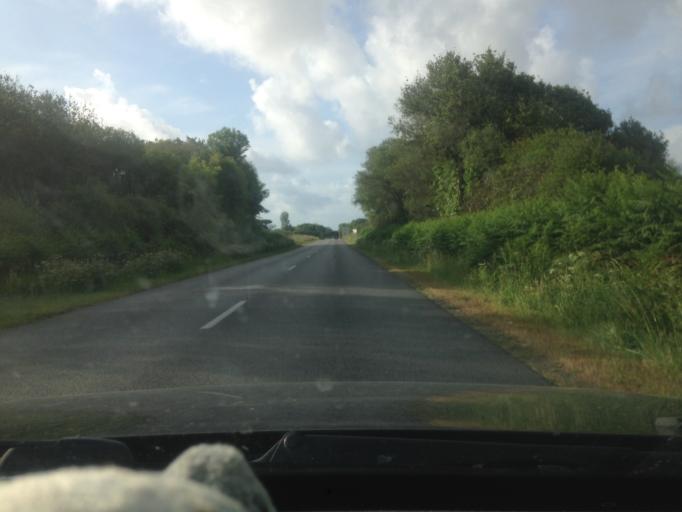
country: FR
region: Brittany
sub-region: Departement du Morbihan
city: Erdeven
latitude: 47.6246
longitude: -3.1394
